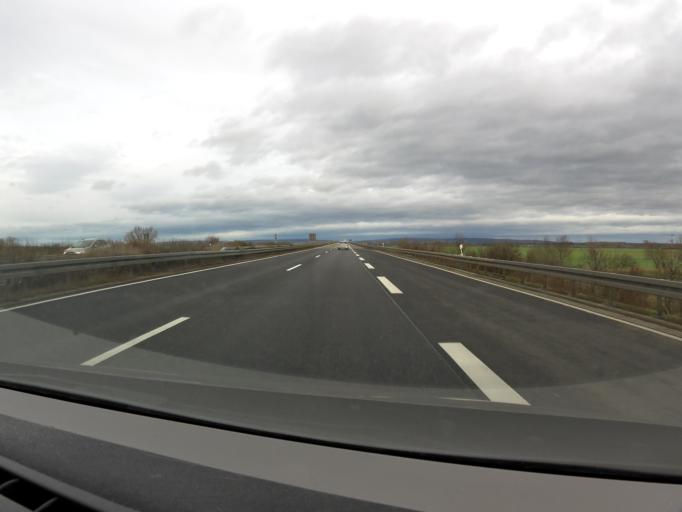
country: DE
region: Thuringia
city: Sprotau
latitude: 51.1581
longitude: 11.1681
